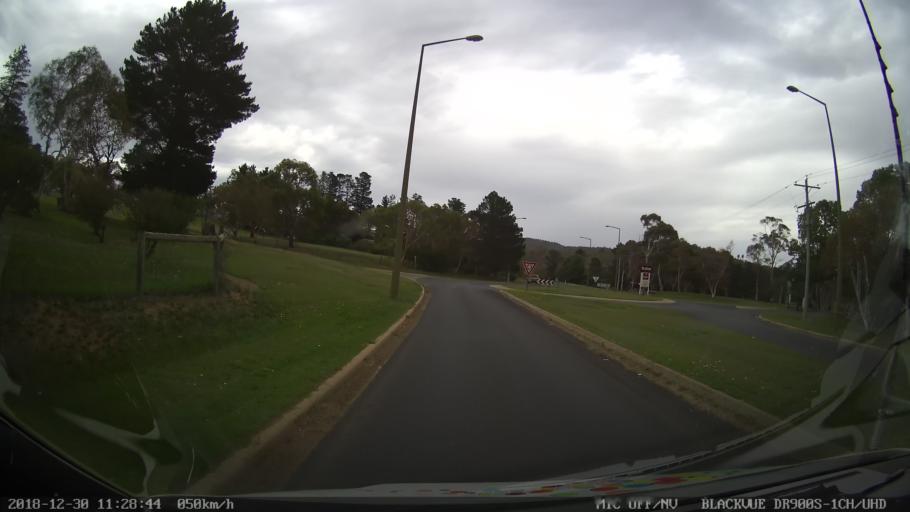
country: AU
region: New South Wales
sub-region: Snowy River
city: Jindabyne
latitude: -36.4520
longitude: 148.6144
